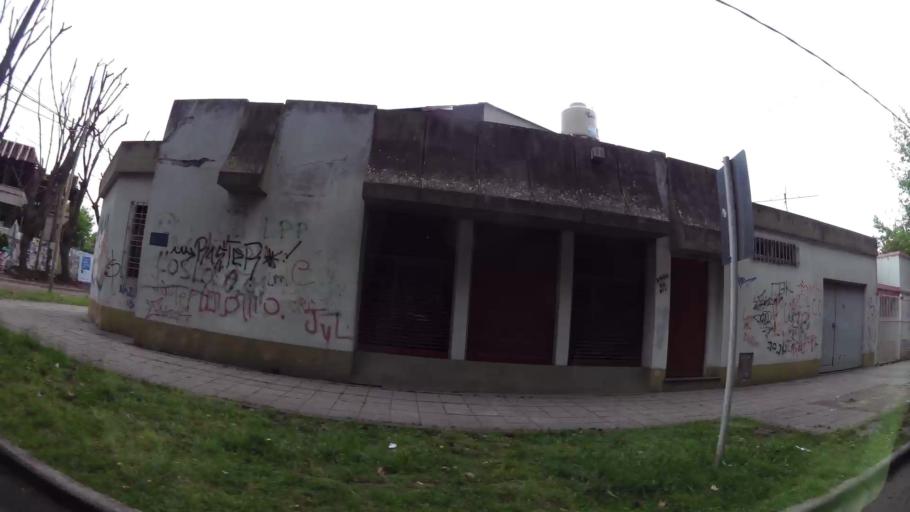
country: AR
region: Buenos Aires
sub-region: Partido de Quilmes
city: Quilmes
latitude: -34.8038
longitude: -58.2765
